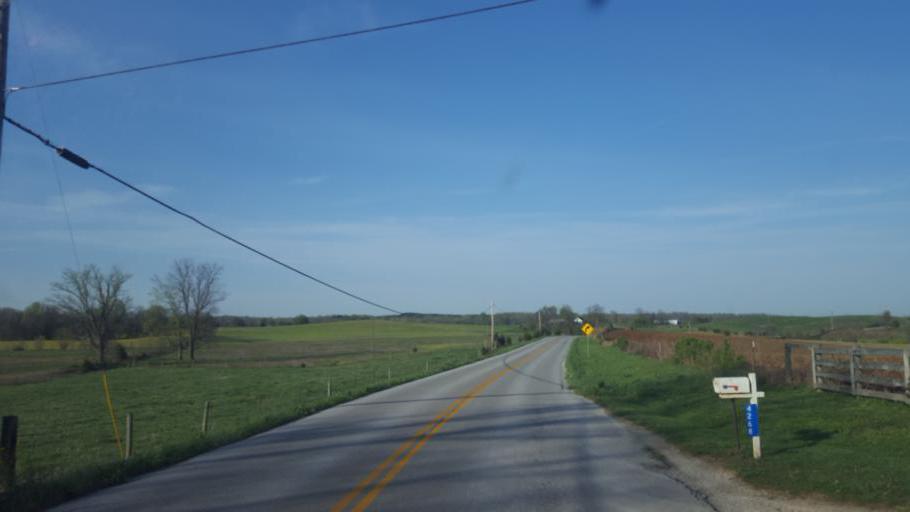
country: US
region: Kentucky
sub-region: Hardin County
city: Elizabethtown
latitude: 37.4963
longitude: -85.9497
